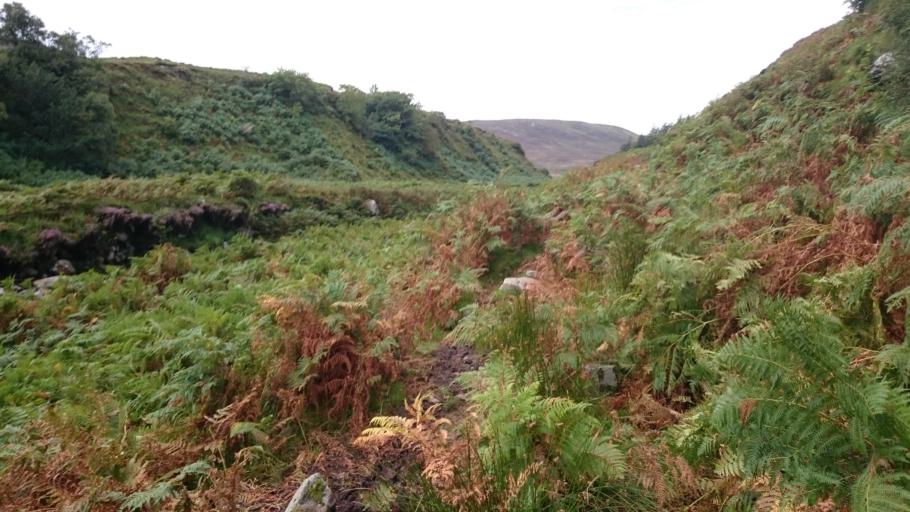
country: IE
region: Connaught
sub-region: Maigh Eo
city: Westport
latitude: 53.9891
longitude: -9.5798
